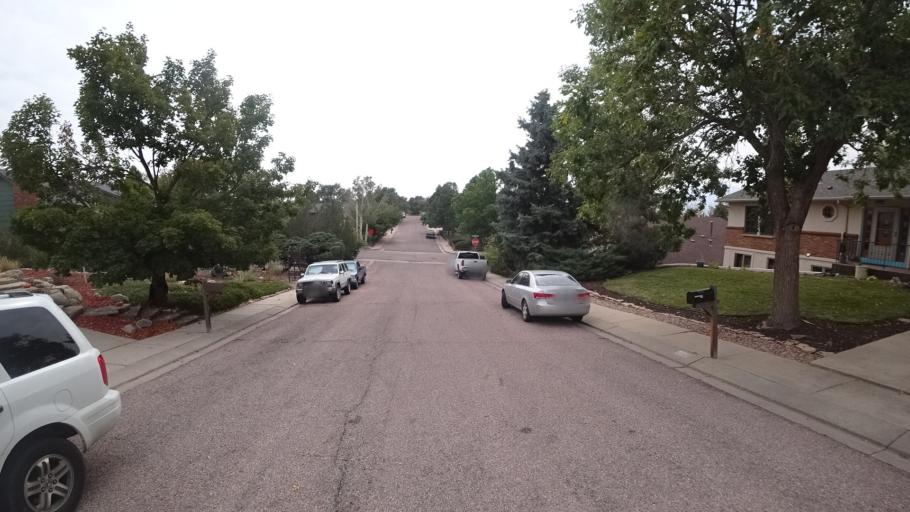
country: US
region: Colorado
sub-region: El Paso County
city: Cimarron Hills
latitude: 38.9009
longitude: -104.7245
